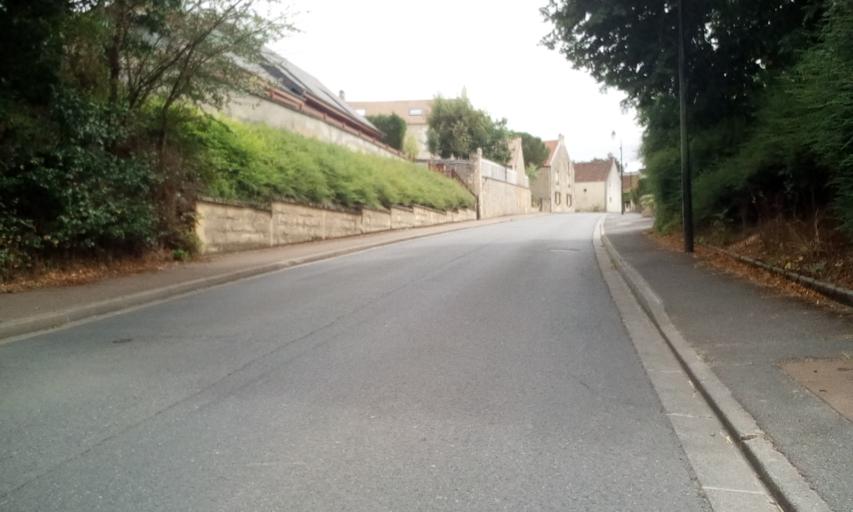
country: FR
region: Lower Normandy
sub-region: Departement du Calvados
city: Fontaine-Etoupefour
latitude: 49.1491
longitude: -0.4559
